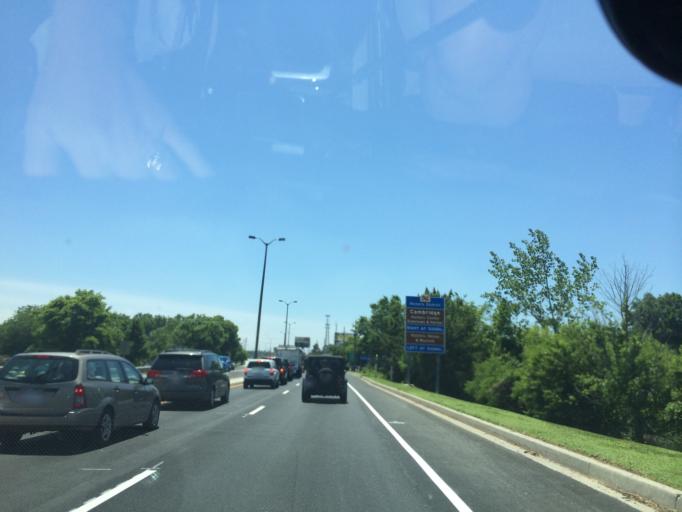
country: US
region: Maryland
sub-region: Dorchester County
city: Cambridge
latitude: 38.5716
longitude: -76.0631
